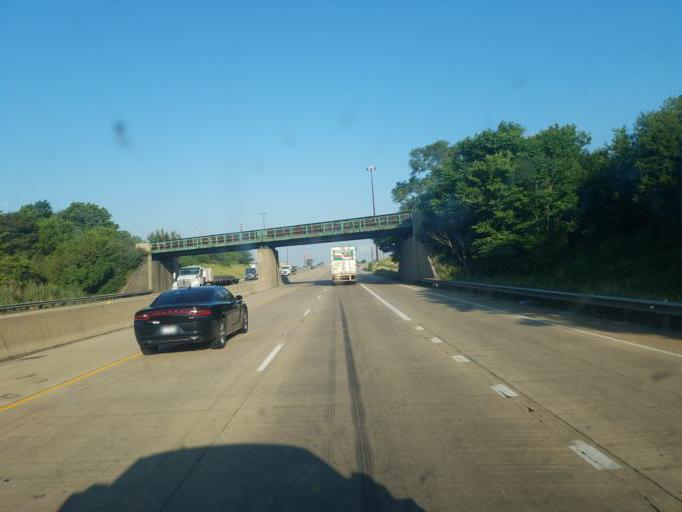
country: US
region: Illinois
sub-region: Grundy County
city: Minooka
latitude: 41.4626
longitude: -88.2627
